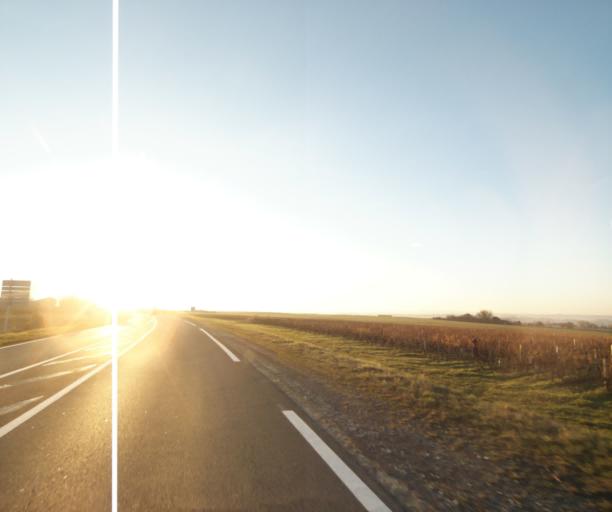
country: FR
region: Poitou-Charentes
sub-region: Departement de la Charente-Maritime
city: Cherac
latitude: 45.7109
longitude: -0.4910
